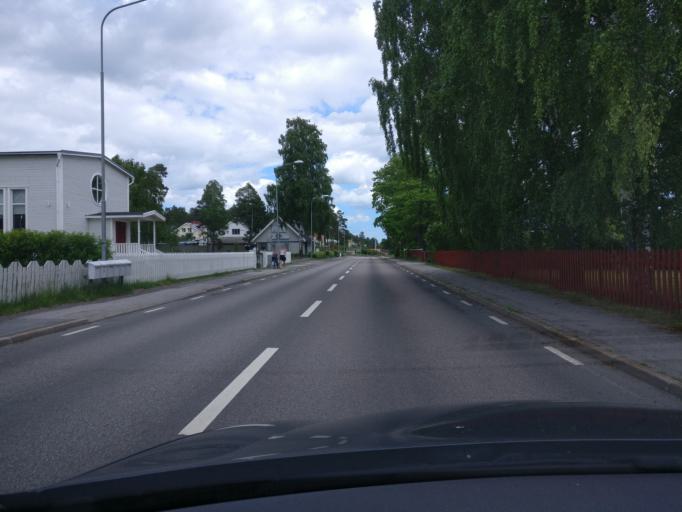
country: SE
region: Kalmar
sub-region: Vasterviks Kommun
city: Vaestervik
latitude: 57.9029
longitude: 16.6909
